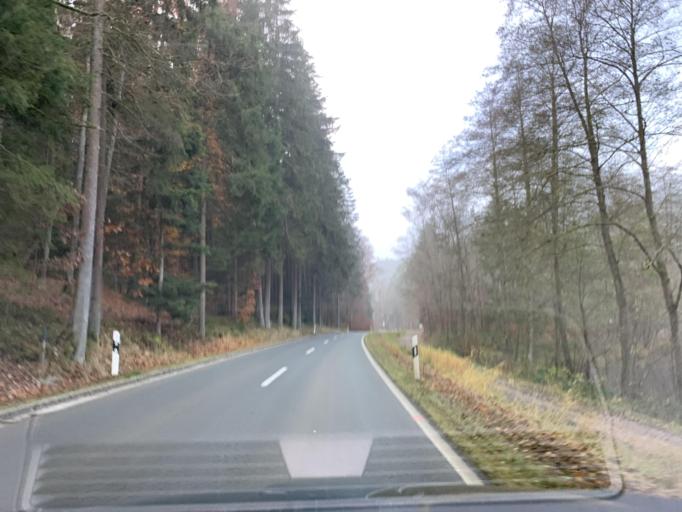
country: DE
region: Bavaria
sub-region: Upper Palatinate
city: Neunburg vorm Wald
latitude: 49.3711
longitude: 12.4113
